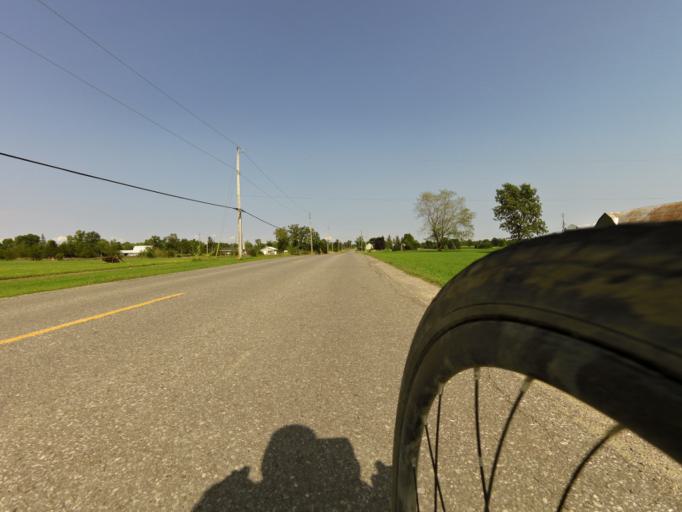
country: CA
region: Ontario
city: Skatepark
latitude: 44.2449
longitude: -76.7307
